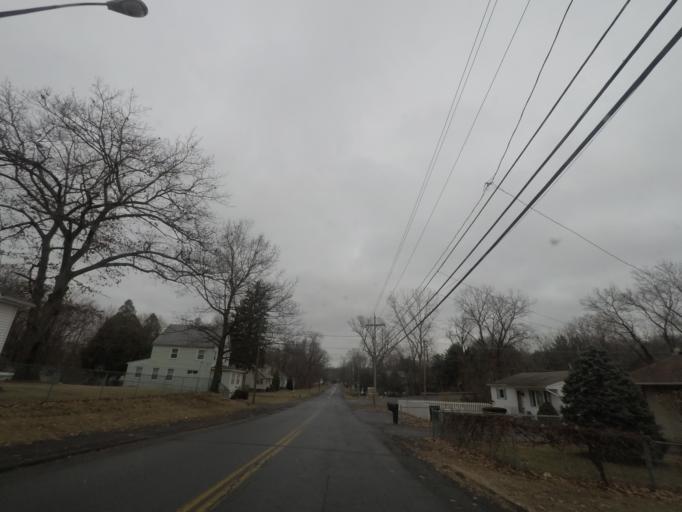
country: US
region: New York
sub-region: Saratoga County
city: Waterford
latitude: 42.7924
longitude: -73.6644
